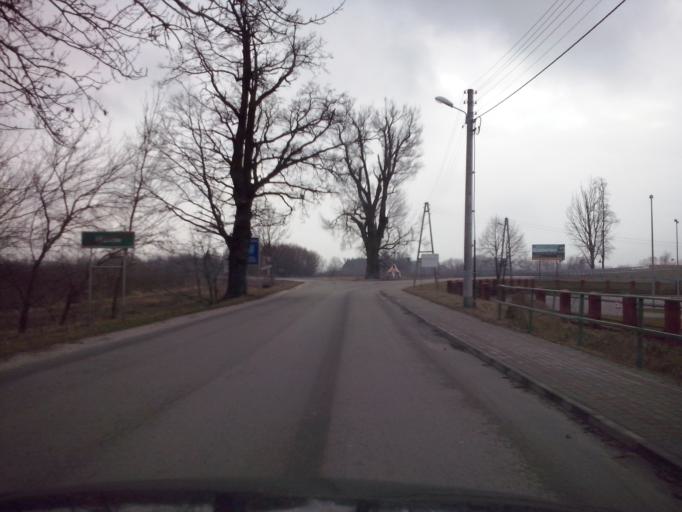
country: PL
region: Subcarpathian Voivodeship
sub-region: Powiat nizanski
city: Ulanow
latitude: 50.4878
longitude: 22.2658
